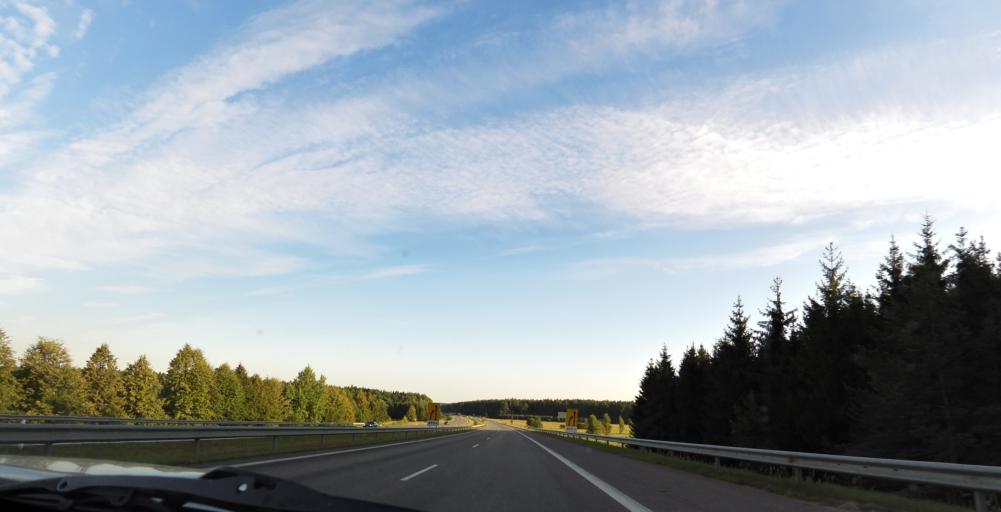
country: LT
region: Vilnius County
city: Ukmerge
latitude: 55.2359
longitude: 24.8211
